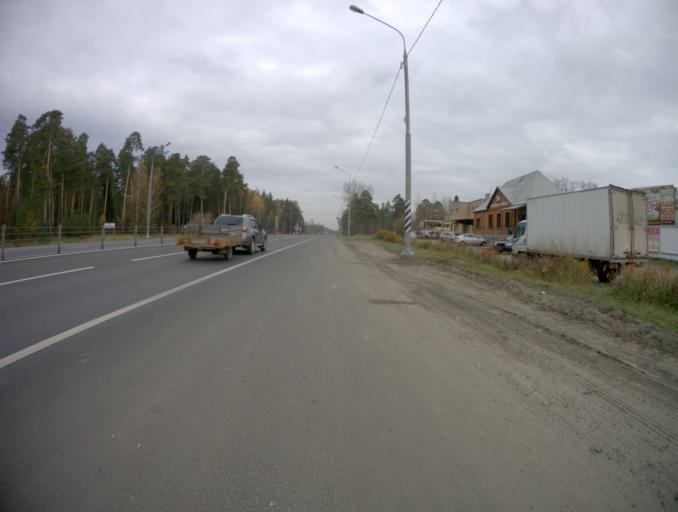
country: RU
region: Moskovskaya
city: Malaya Dubna
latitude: 55.8444
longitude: 38.9654
